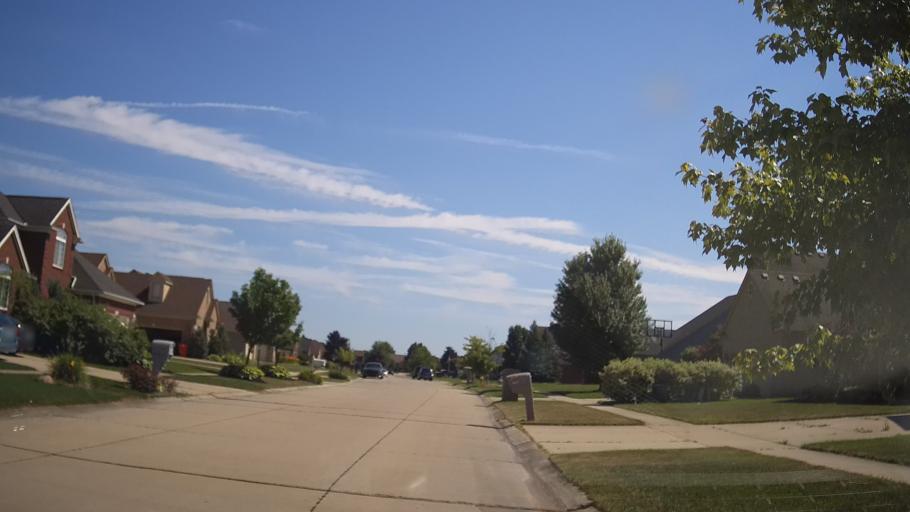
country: US
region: Michigan
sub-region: Macomb County
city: Clinton
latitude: 42.6521
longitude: -82.9149
